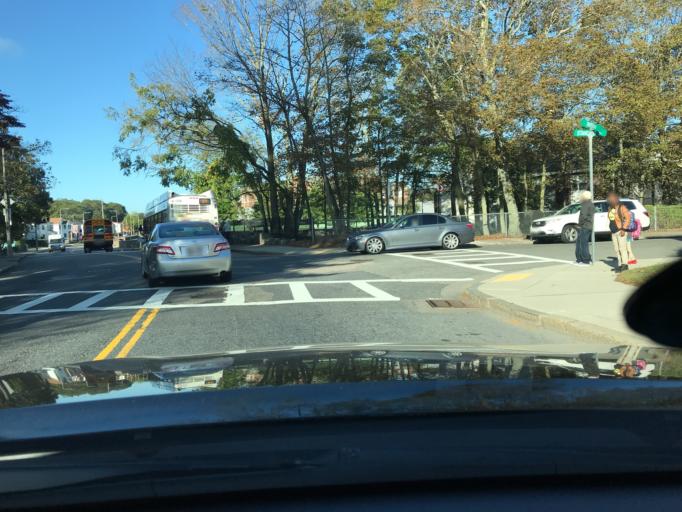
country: US
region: Massachusetts
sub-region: Norfolk County
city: Milton
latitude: 42.2717
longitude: -71.0782
